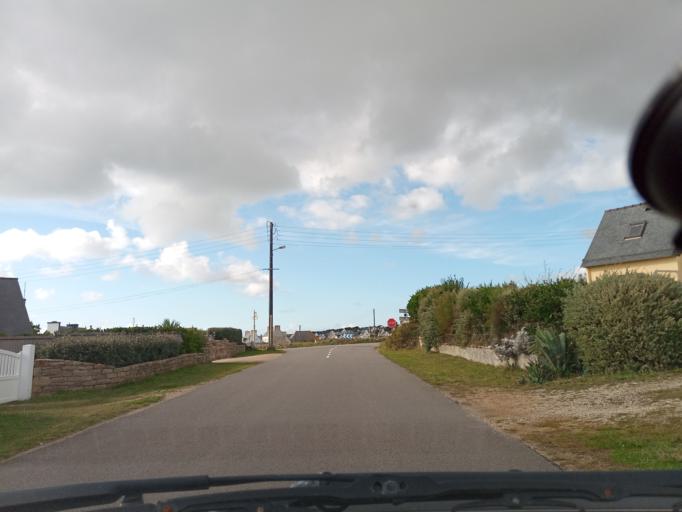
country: FR
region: Brittany
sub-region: Departement du Finistere
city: Plozevet
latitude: 47.9776
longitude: -4.4462
